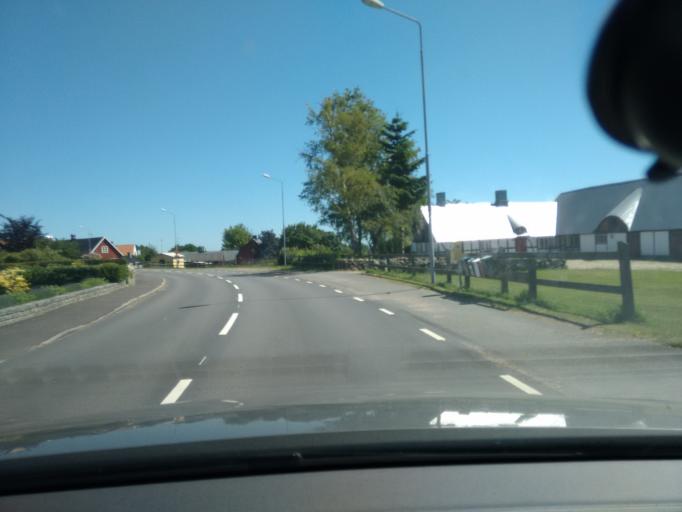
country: SE
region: Skane
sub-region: Kristianstads Kommun
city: Degeberga
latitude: 55.7718
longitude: 14.1486
